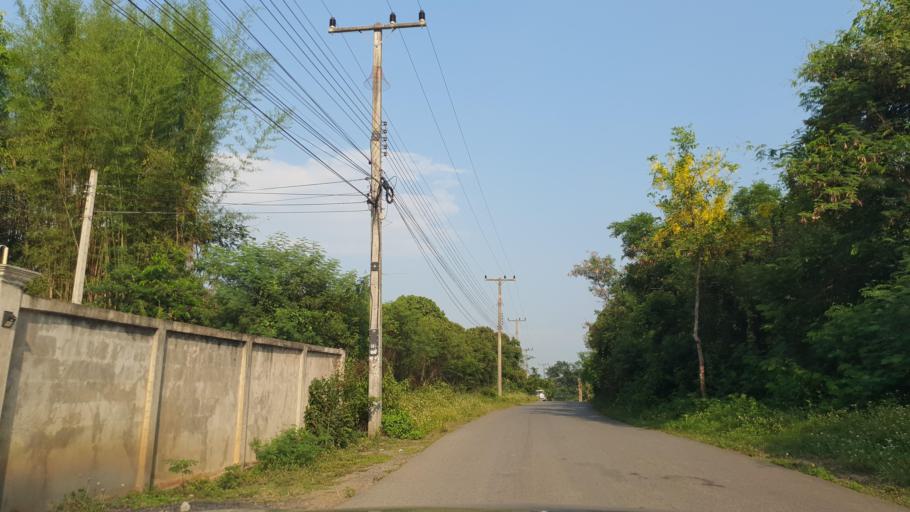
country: TH
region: Chiang Mai
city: Mae Wang
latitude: 18.6674
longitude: 98.8166
